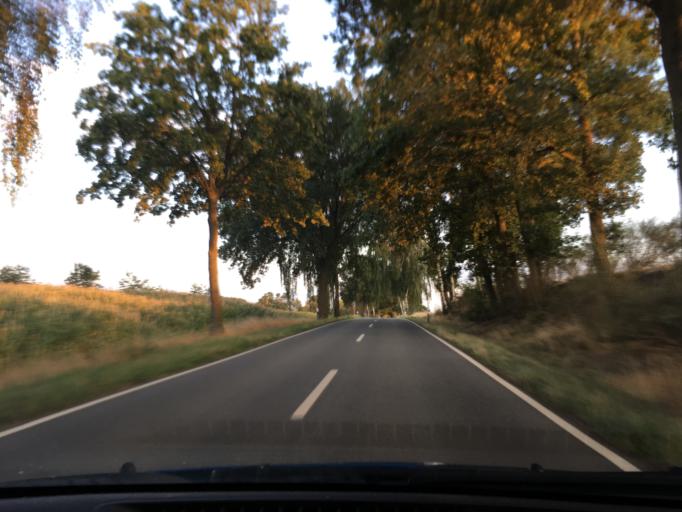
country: DE
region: Lower Saxony
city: Tosterglope
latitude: 53.2196
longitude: 10.8120
